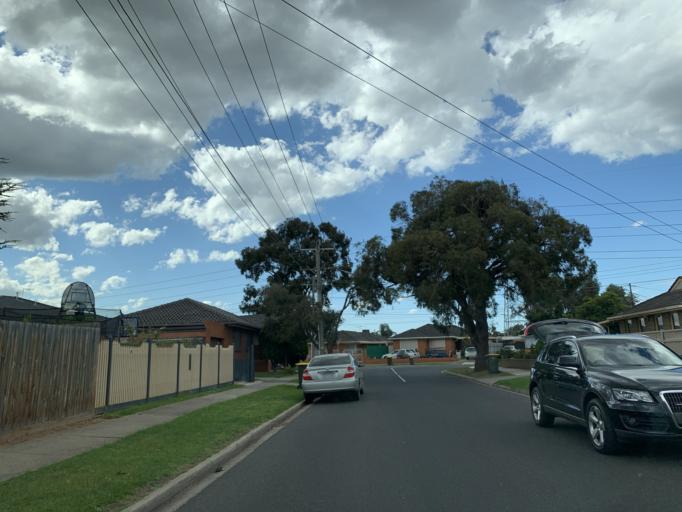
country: AU
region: Victoria
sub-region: Moonee Valley
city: Keilor East
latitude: -37.7431
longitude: 144.8623
